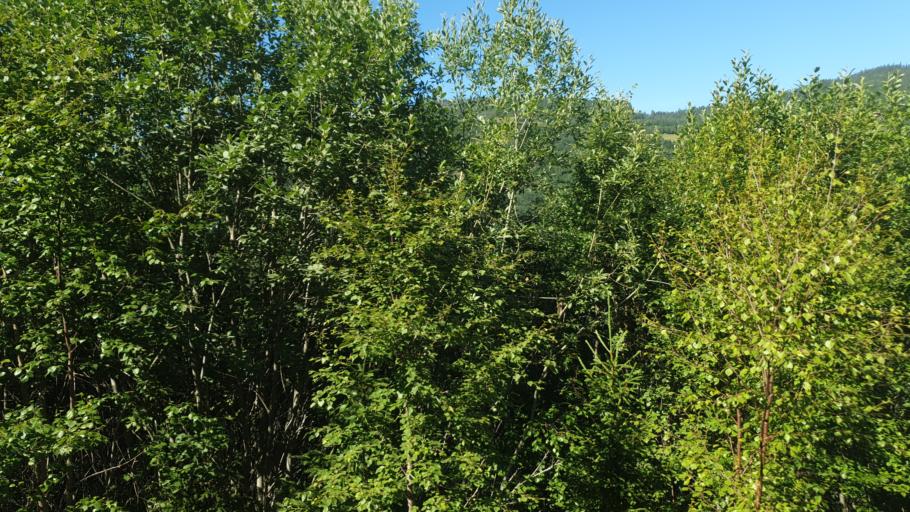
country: NO
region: Sor-Trondelag
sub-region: Meldal
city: Meldal
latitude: 63.1610
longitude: 9.7320
